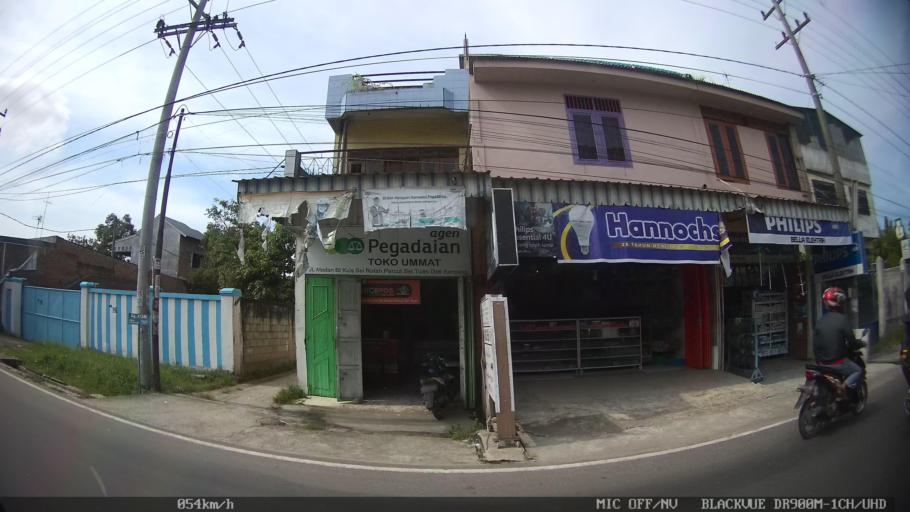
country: ID
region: North Sumatra
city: Percut
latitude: 3.6073
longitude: 98.7732
